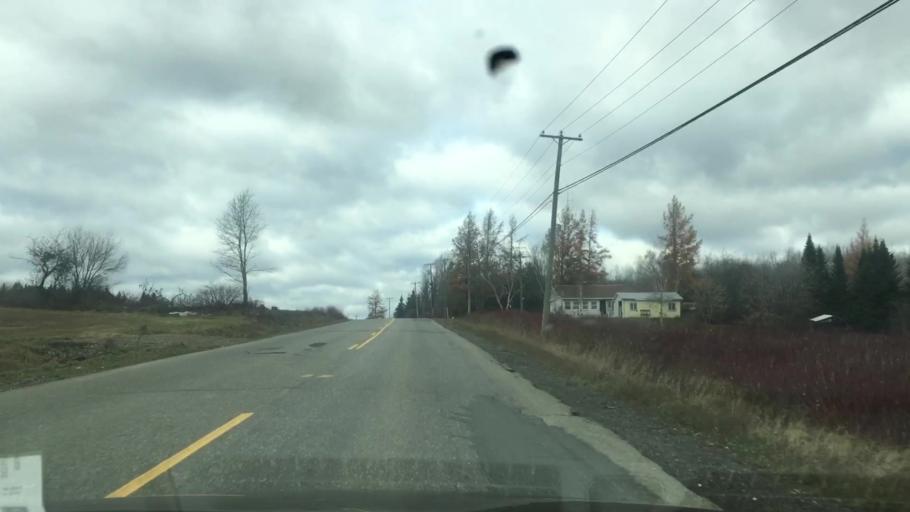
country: US
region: Maine
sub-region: Aroostook County
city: Fort Fairfield
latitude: 46.7532
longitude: -67.7586
